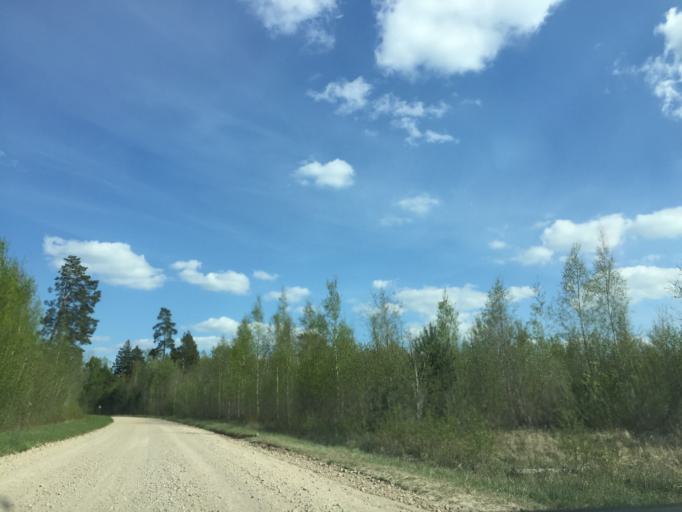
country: LV
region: Vecumnieki
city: Vecumnieki
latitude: 56.5110
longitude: 24.4161
